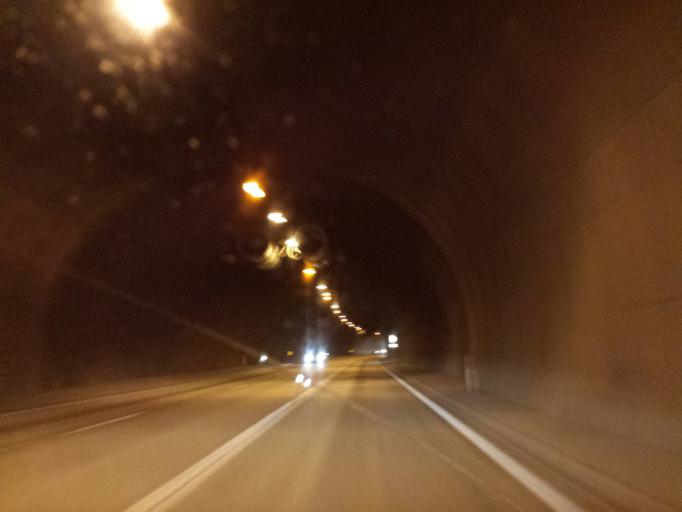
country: IS
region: West
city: Akranes
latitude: 64.3101
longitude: -21.9031
